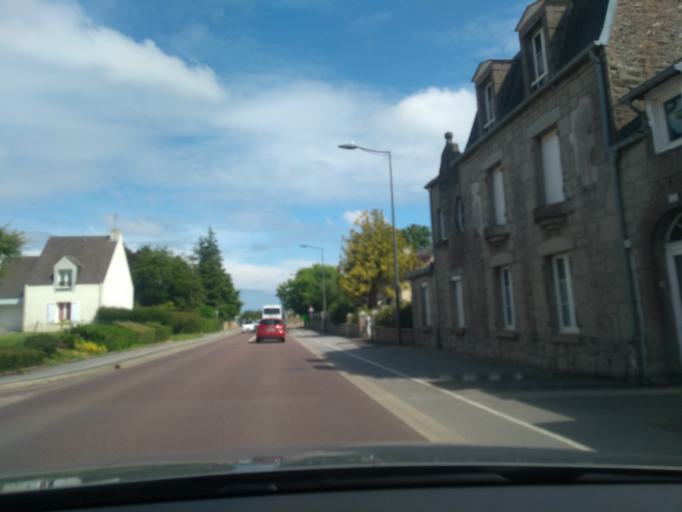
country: FR
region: Lower Normandy
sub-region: Departement de la Manche
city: Quettehou
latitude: 49.5917
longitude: -1.2972
